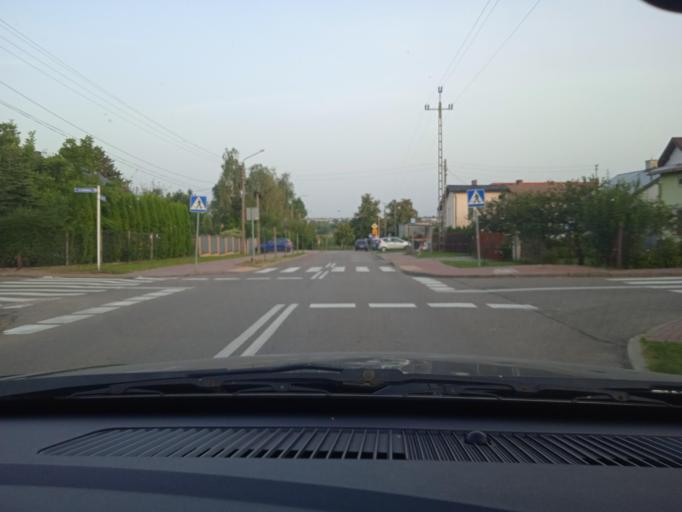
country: PL
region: Masovian Voivodeship
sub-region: Powiat nowodworski
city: Nowy Dwor Mazowiecki
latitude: 52.4445
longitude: 20.7012
